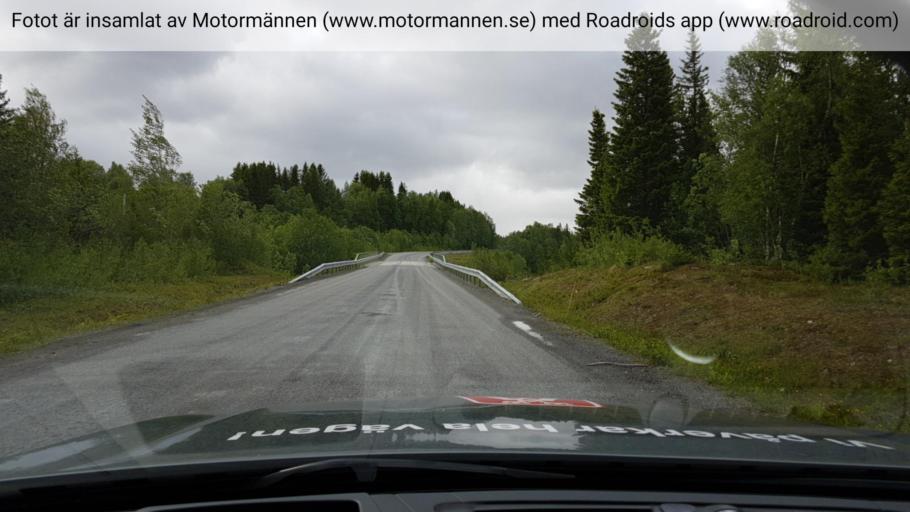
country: SE
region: Jaemtland
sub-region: Are Kommun
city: Are
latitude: 63.7092
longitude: 12.6396
